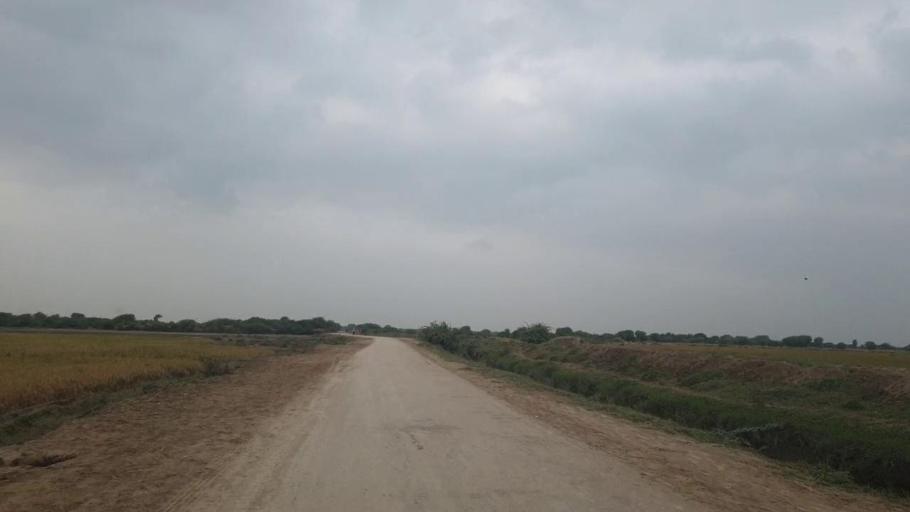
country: PK
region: Sindh
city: Badin
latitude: 24.6410
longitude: 68.6816
